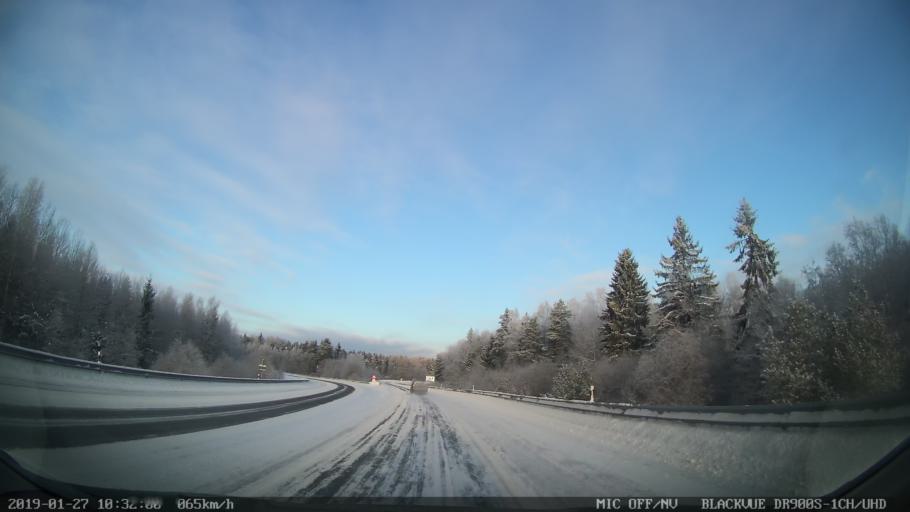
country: EE
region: Harju
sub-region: Raasiku vald
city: Raasiku
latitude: 59.4370
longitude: 25.1895
